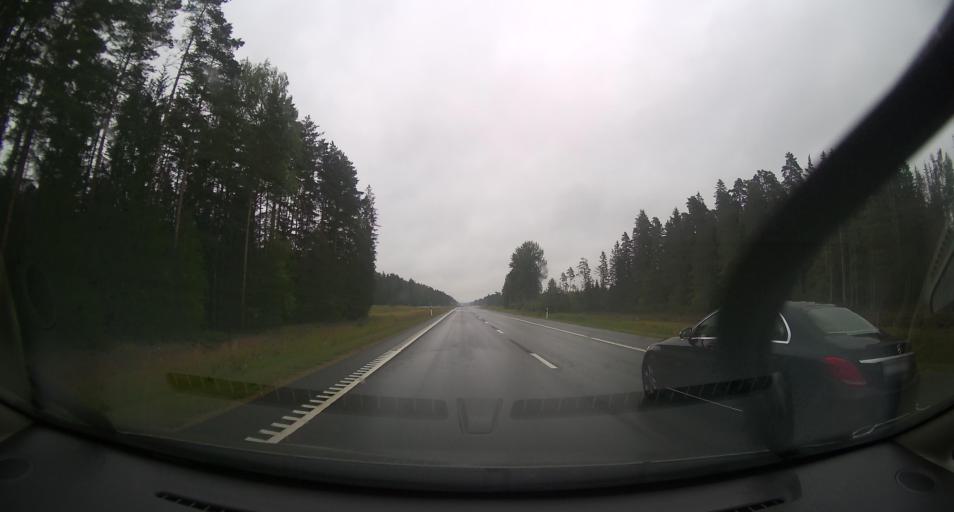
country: EE
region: Harju
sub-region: Loksa linn
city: Loksa
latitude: 59.4566
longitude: 25.8538
